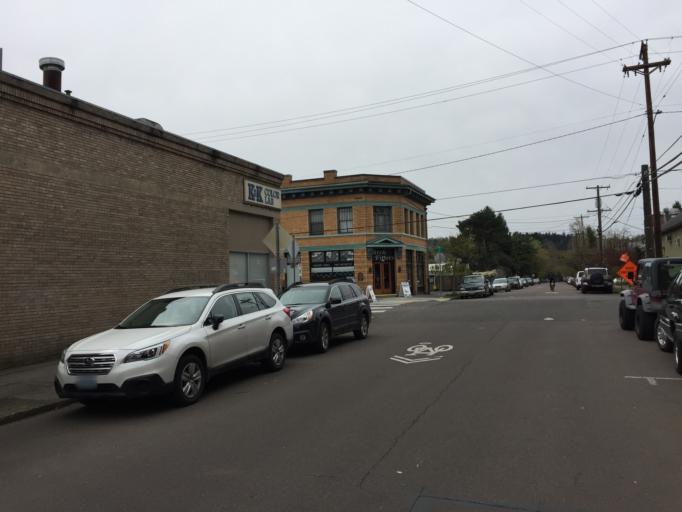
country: US
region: Oregon
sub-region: Clackamas County
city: Milwaukie
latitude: 45.4629
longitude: -122.6526
